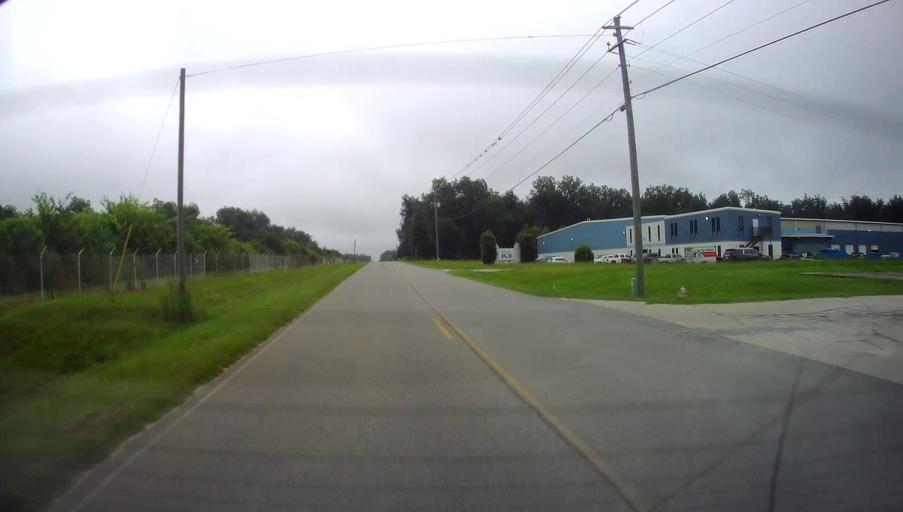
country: US
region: Georgia
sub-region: Peach County
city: Byron
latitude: 32.6520
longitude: -83.7358
